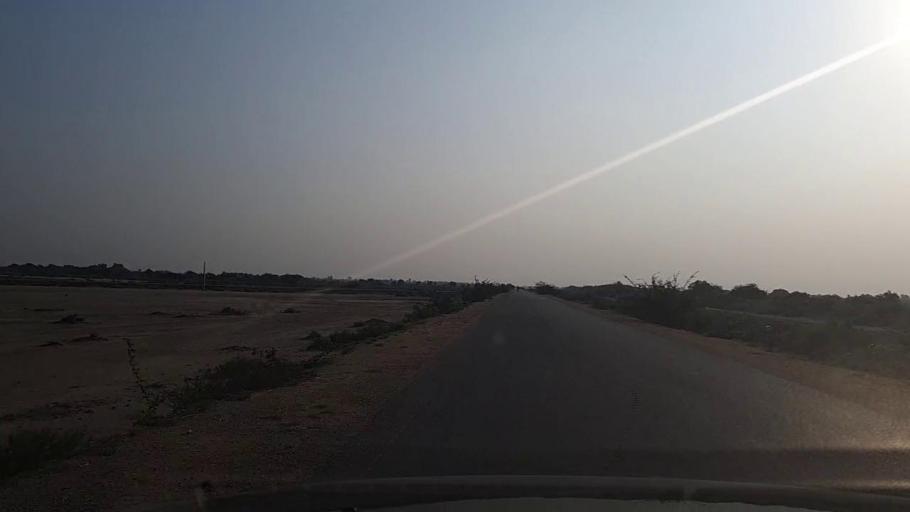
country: PK
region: Sindh
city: Mirpur Sakro
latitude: 24.5180
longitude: 67.8221
